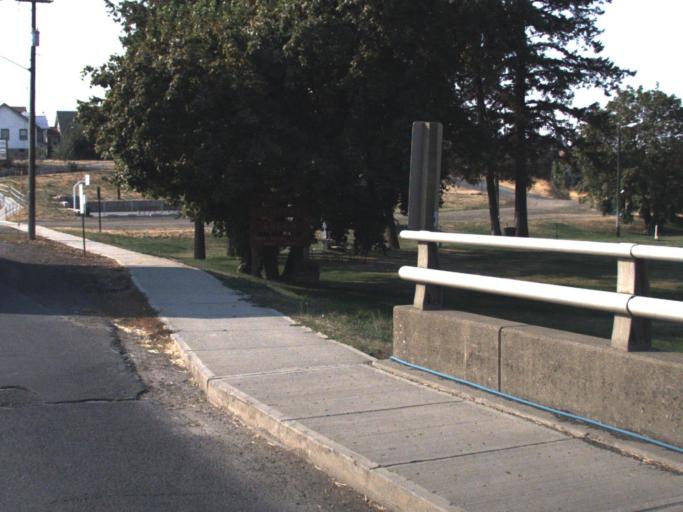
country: US
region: Idaho
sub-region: Benewah County
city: Plummer
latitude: 47.2263
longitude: -117.0729
